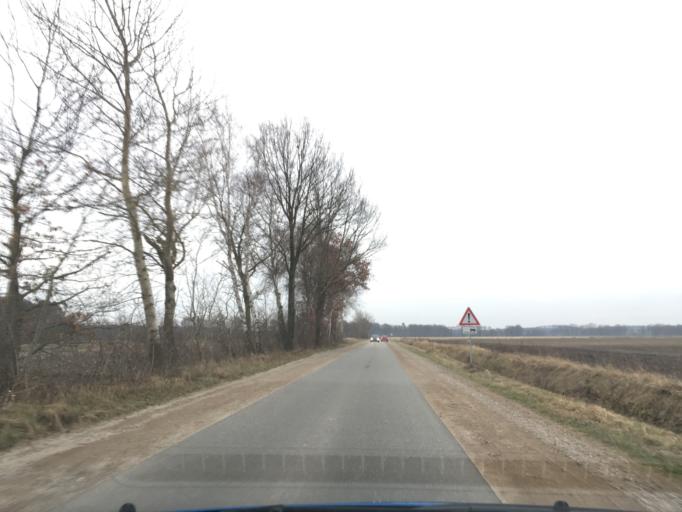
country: DE
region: Lower Saxony
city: Mechtersen
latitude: 53.3006
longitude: 10.3287
